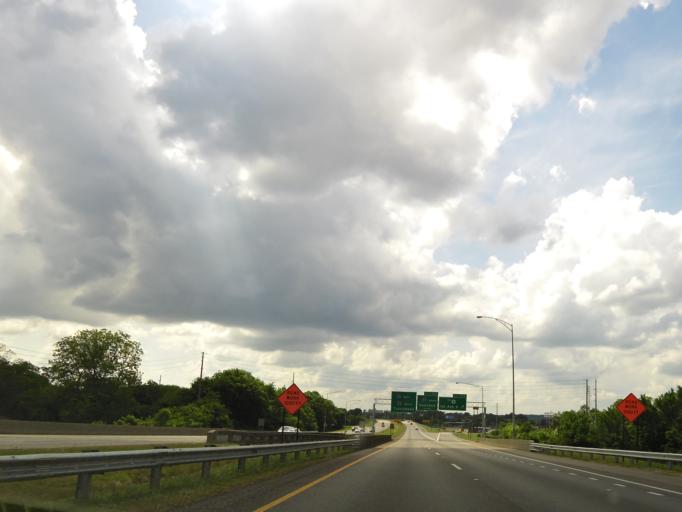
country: US
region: Alabama
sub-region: Jefferson County
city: Irondale
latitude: 33.5434
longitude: -86.7380
